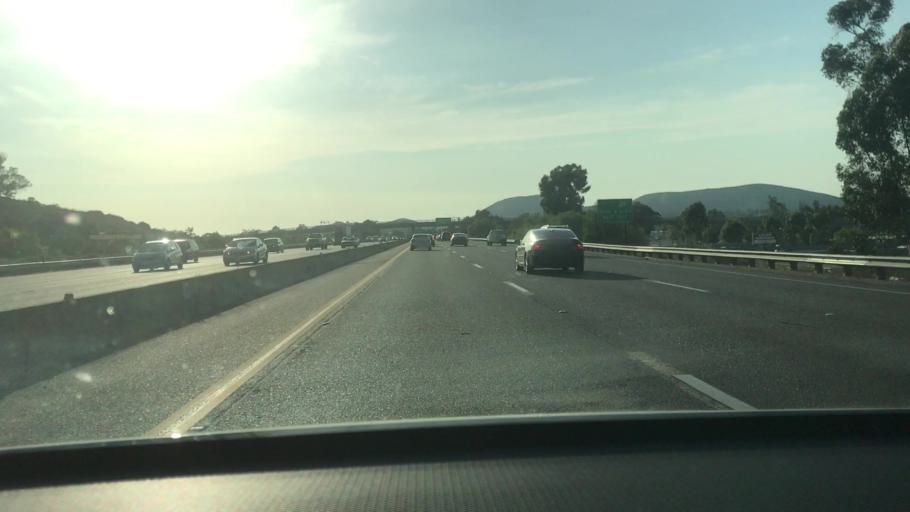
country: US
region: California
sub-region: San Diego County
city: San Marcos
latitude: 33.1373
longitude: -117.1368
